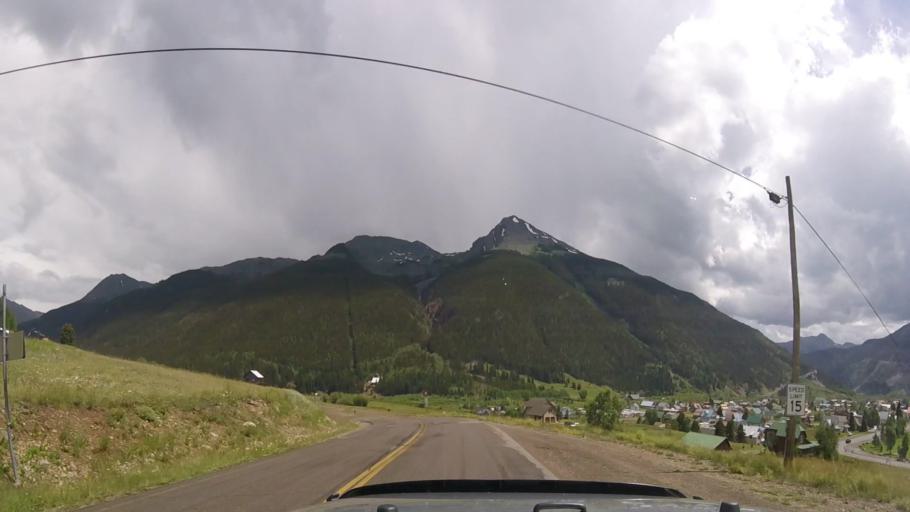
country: US
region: Colorado
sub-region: San Juan County
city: Silverton
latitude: 37.8188
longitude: -107.6591
